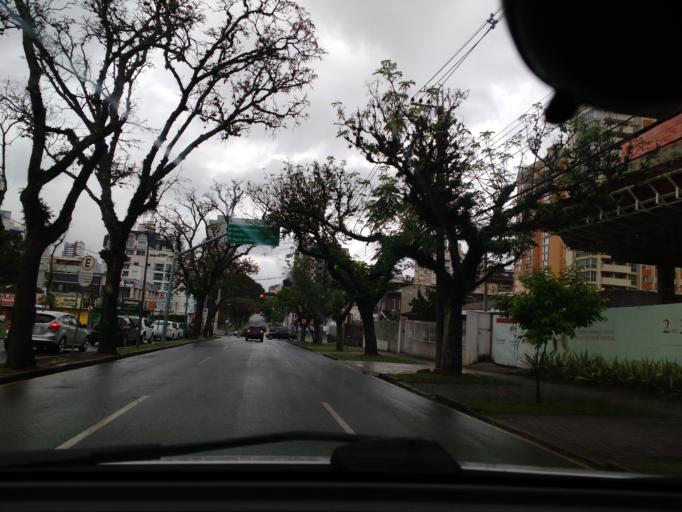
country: BR
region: Parana
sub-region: Curitiba
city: Curitiba
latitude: -25.4282
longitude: -49.2864
